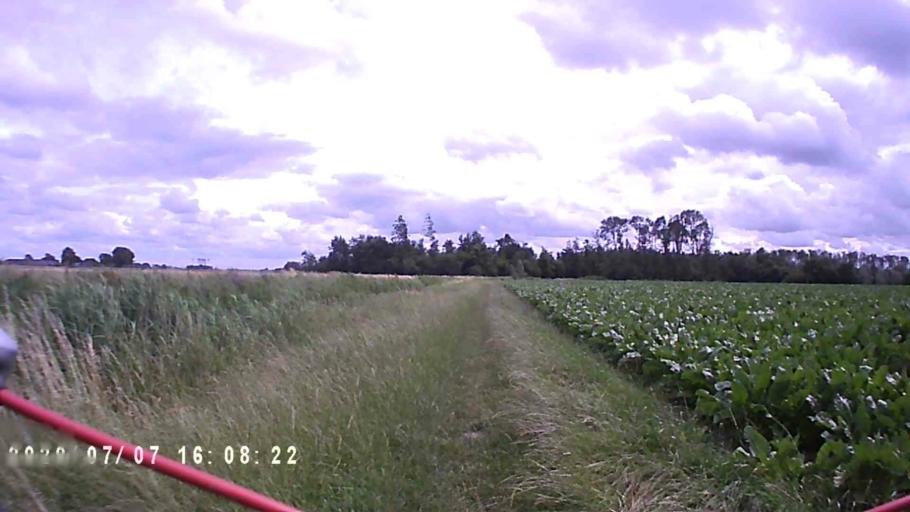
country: NL
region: Groningen
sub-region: Gemeente Winsum
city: Winsum
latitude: 53.3687
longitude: 6.5243
